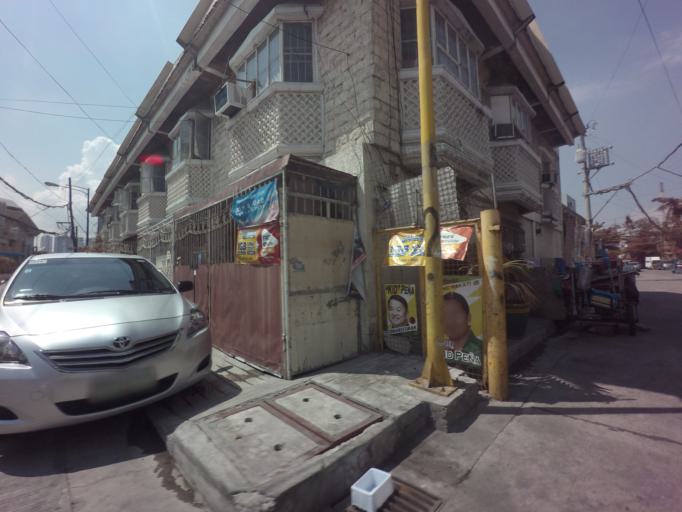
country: PH
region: Metro Manila
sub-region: Makati City
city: Makati City
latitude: 14.5704
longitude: 121.0088
